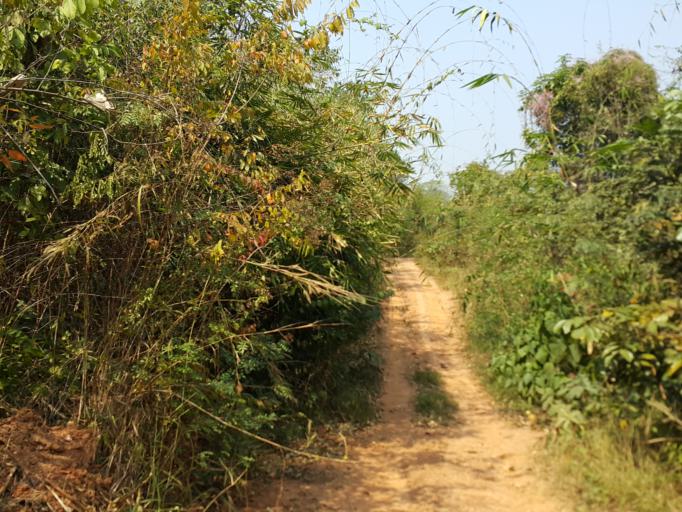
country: TH
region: Sukhothai
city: Thung Saliam
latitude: 17.3249
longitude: 99.4997
